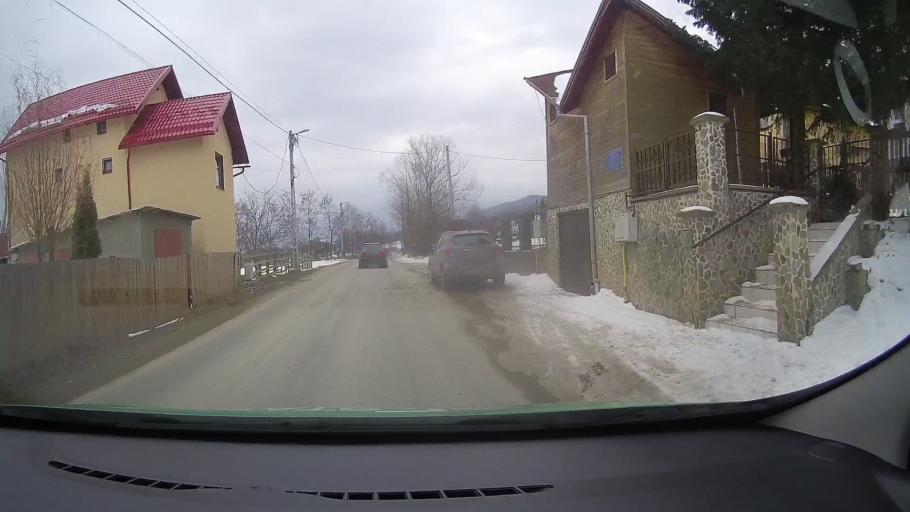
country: RO
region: Brasov
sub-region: Comuna Zarnesti
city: Zarnesti
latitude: 45.5398
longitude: 25.3318
